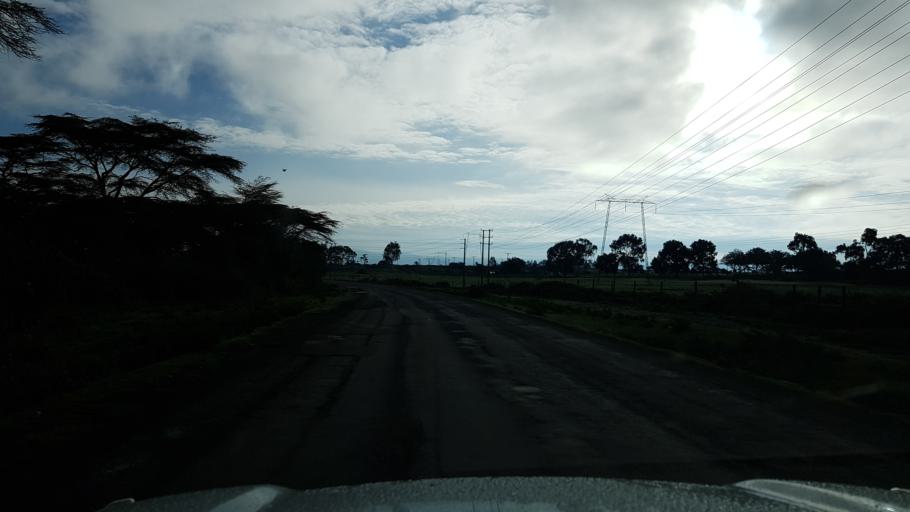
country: KE
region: Nakuru
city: Naivasha
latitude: -0.8234
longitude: 36.3832
